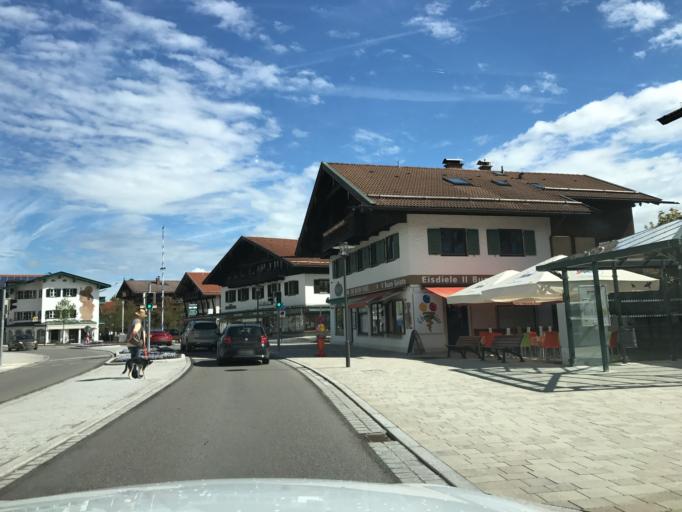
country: DE
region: Bavaria
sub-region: Upper Bavaria
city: Bad Wiessee
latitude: 47.7121
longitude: 11.7255
